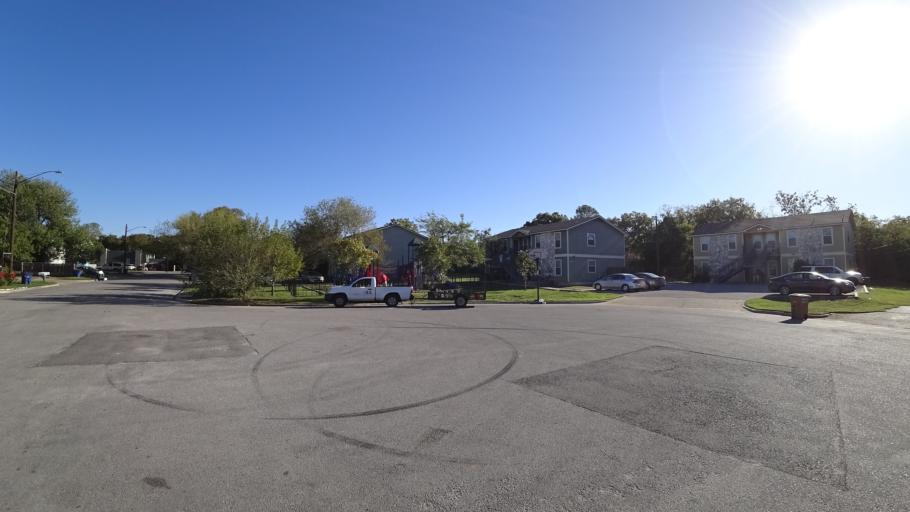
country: US
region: Texas
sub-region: Travis County
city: Austin
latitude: 30.3051
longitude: -97.6796
